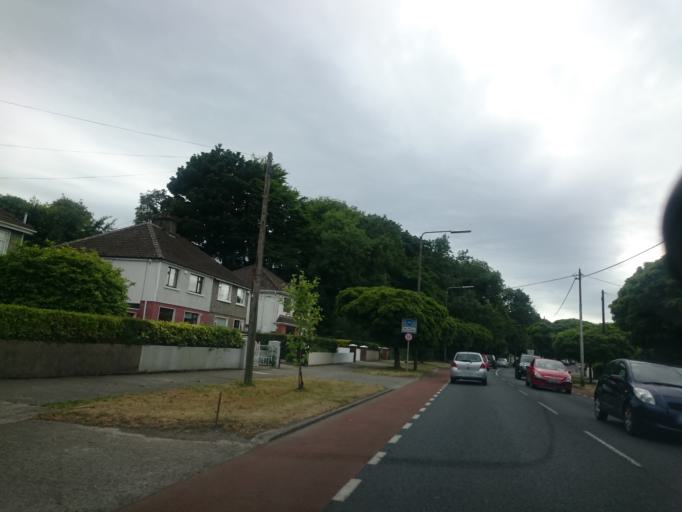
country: IE
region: Leinster
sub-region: South Dublin
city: Terenure
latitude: 53.3039
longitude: -6.2797
